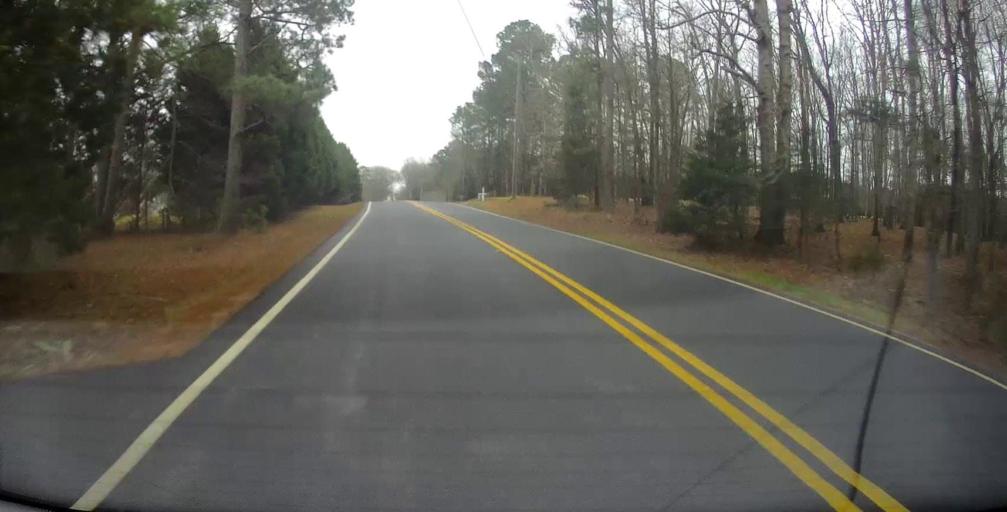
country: US
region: Georgia
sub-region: Pike County
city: Zebulon
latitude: 33.0573
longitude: -84.2729
